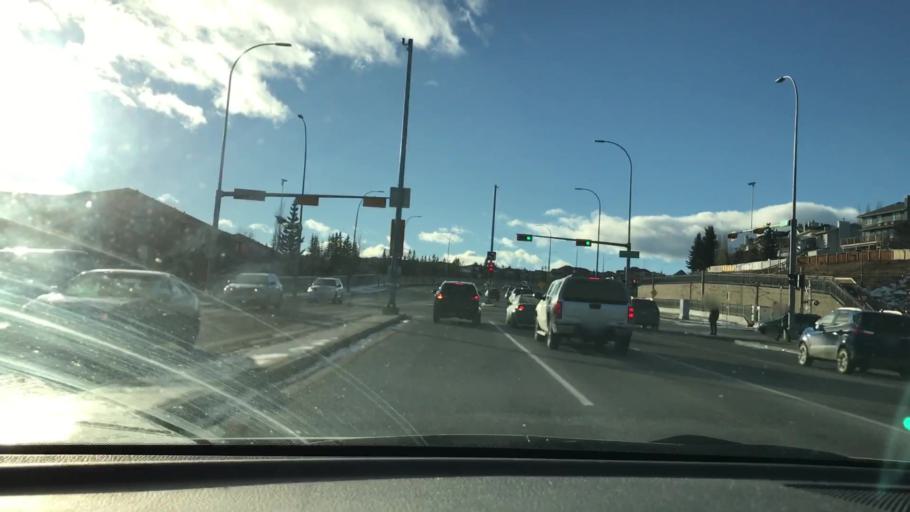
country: CA
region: Alberta
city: Calgary
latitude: 51.0384
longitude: -114.1691
